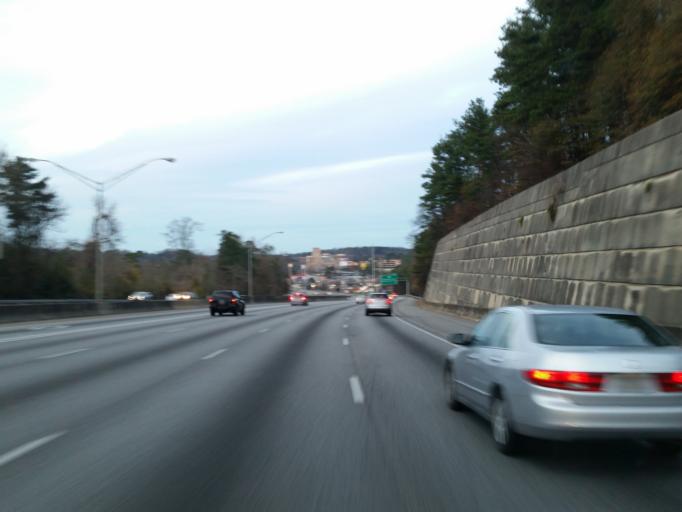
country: US
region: Georgia
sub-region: Cobb County
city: Vinings
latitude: 33.8410
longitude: -84.4299
